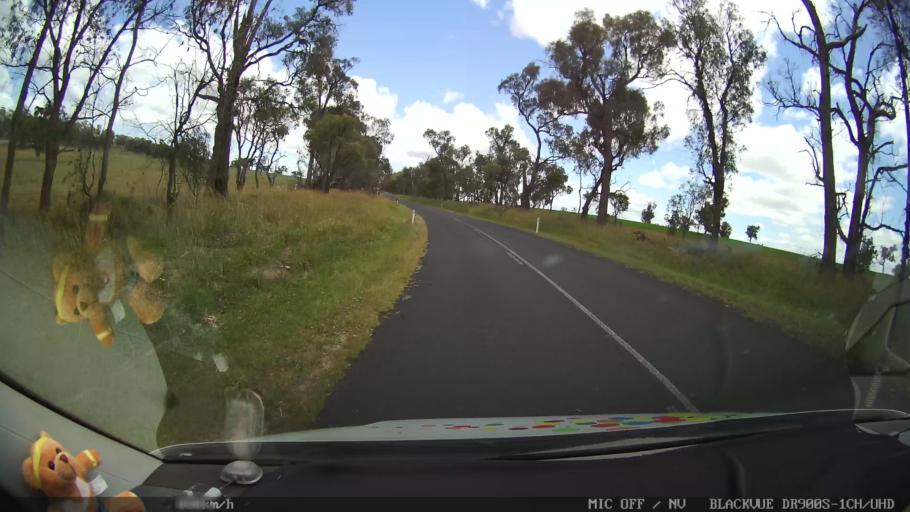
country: AU
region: New South Wales
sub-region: Glen Innes Severn
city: Glen Innes
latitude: -29.4843
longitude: 151.6844
